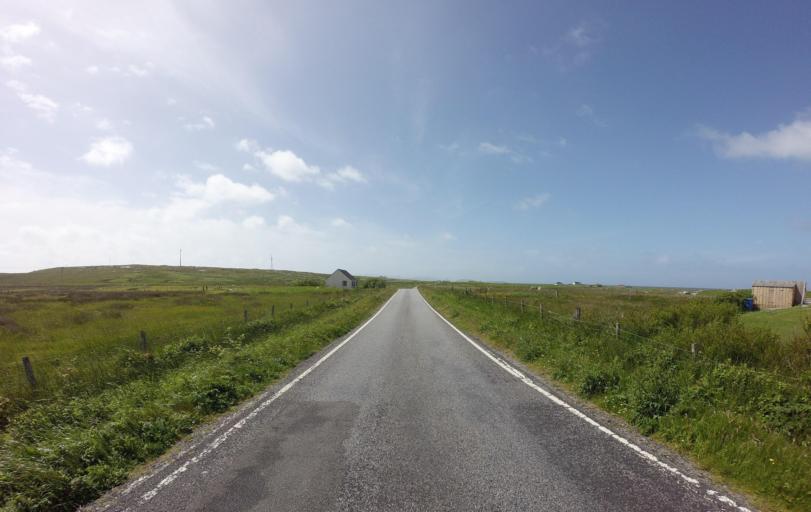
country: GB
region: Scotland
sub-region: Eilean Siar
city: Isle of South Uist
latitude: 57.1149
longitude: -7.3657
